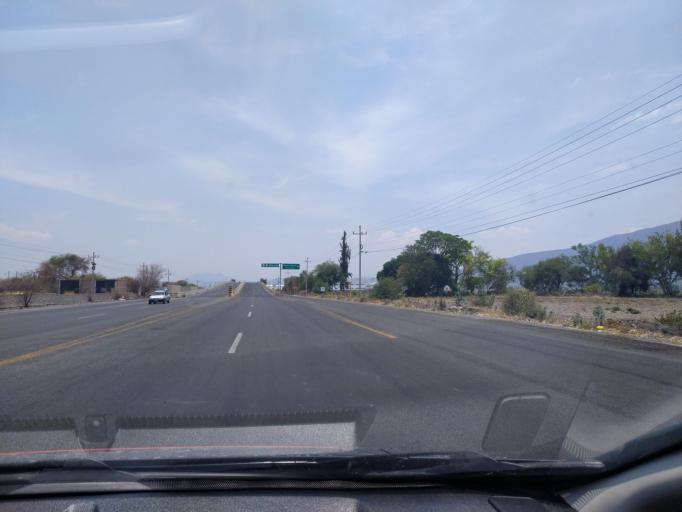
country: MX
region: Jalisco
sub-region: Acatlan de Juarez
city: Villa de los Ninos
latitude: 20.3379
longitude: -103.5906
